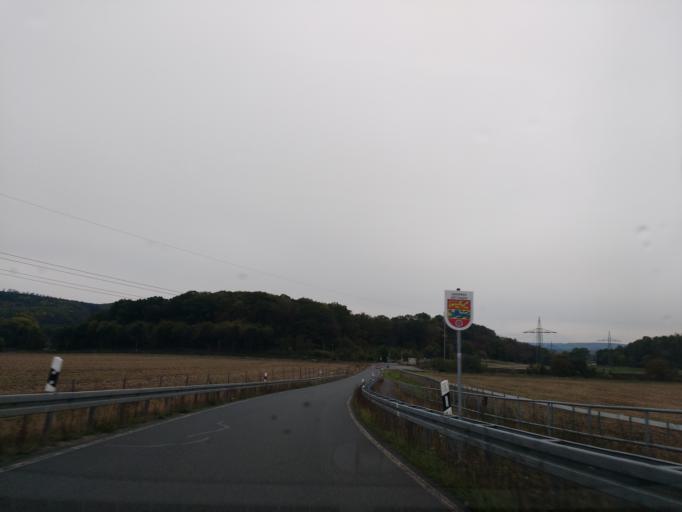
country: DE
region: Lower Saxony
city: Gemeinde Friedland
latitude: 51.4099
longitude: 9.9121
